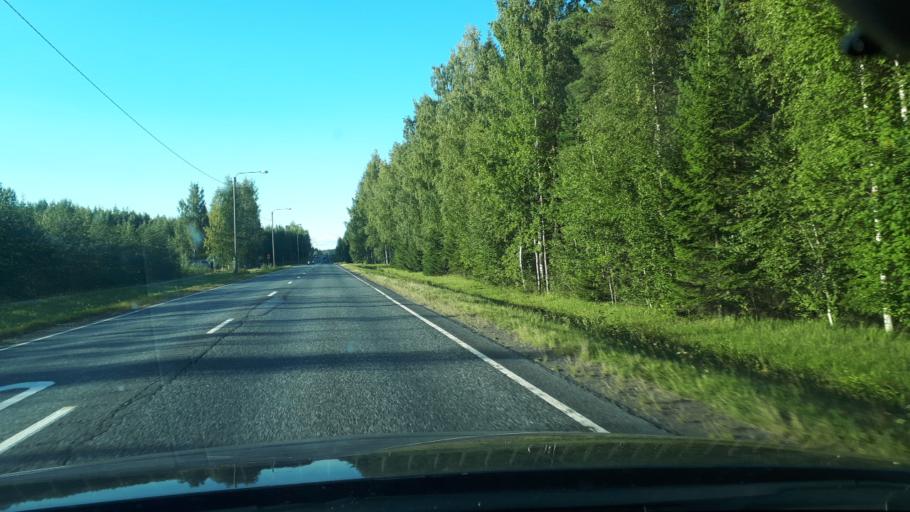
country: FI
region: Northern Savo
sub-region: Ylae-Savo
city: Lapinlahti
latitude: 63.4272
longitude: 27.3291
